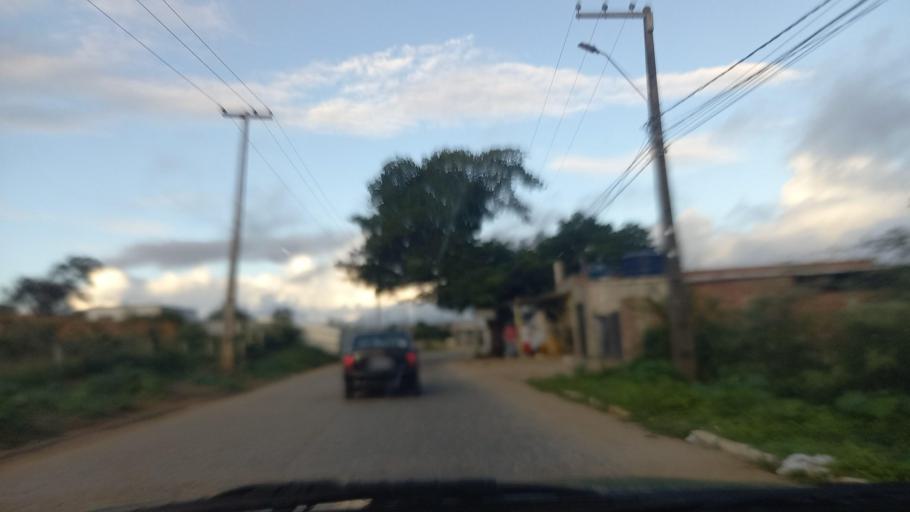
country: BR
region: Pernambuco
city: Garanhuns
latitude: -8.8906
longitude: -36.4501
